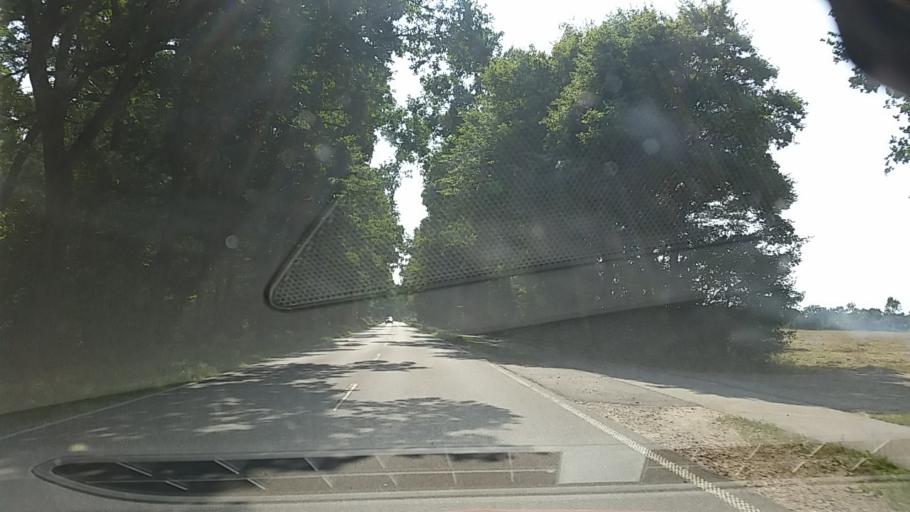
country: DE
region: Schleswig-Holstein
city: Witzhave
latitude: 53.5721
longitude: 10.3510
